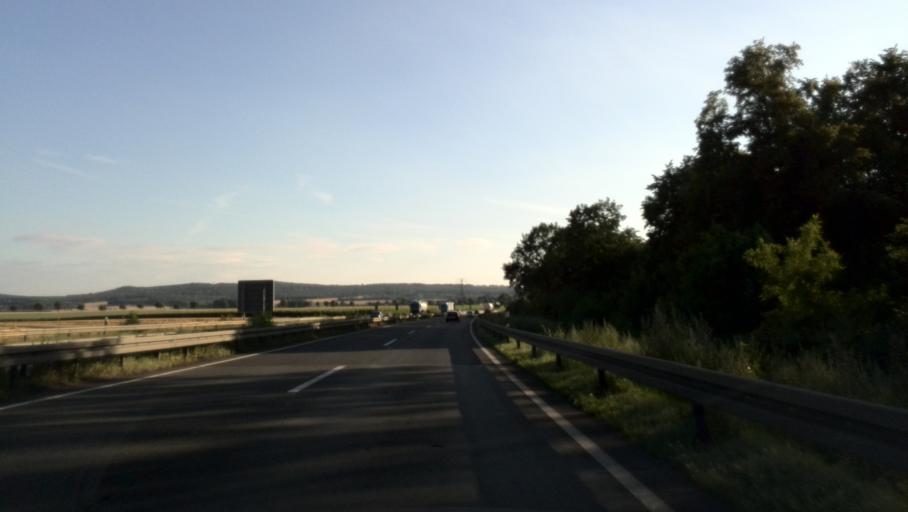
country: DE
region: Lower Saxony
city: Lengede
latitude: 52.1495
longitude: 10.3582
